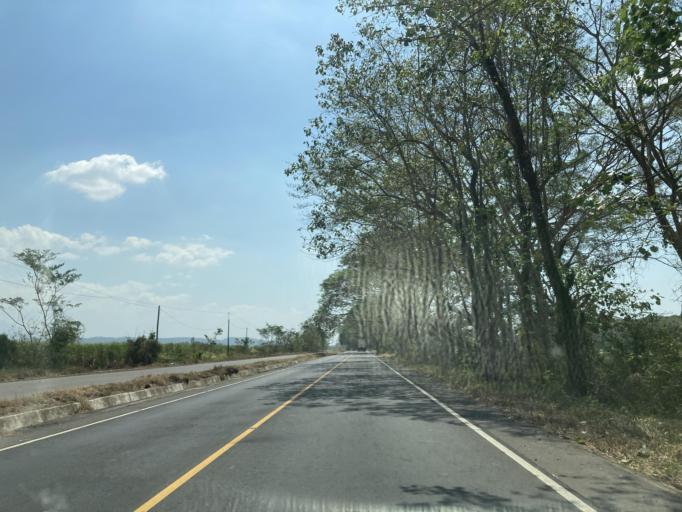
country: GT
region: Escuintla
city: Guanagazapa
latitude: 14.2023
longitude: -90.7038
